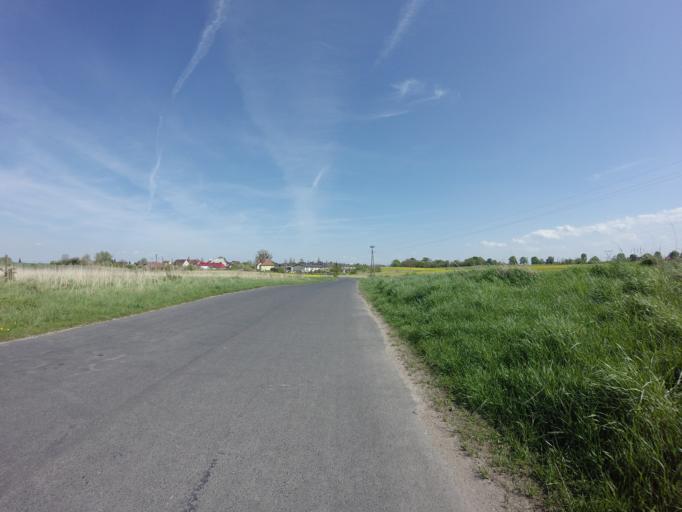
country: PL
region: West Pomeranian Voivodeship
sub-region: Powiat choszczenski
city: Choszczno
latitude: 53.1638
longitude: 15.3924
